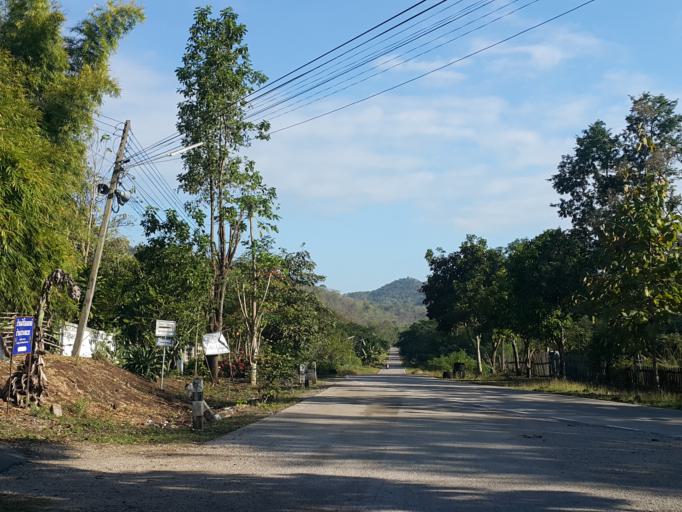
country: TH
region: Lampang
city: Mae Mo
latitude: 18.2691
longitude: 99.6310
